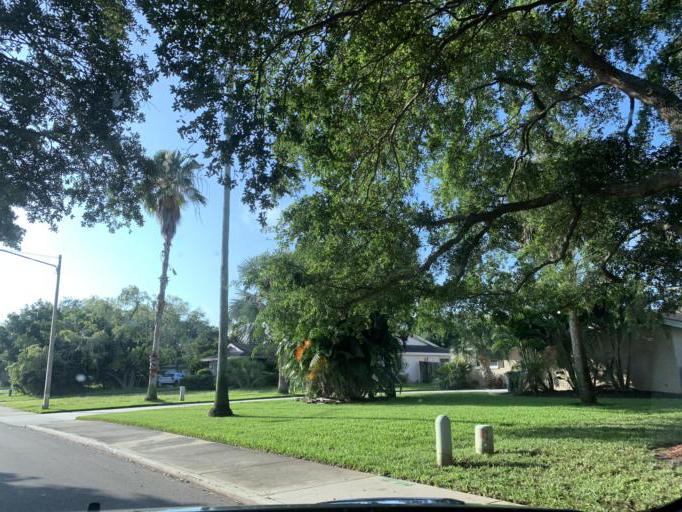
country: US
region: Florida
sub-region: Pinellas County
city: Gandy
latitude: 27.8177
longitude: -82.6084
